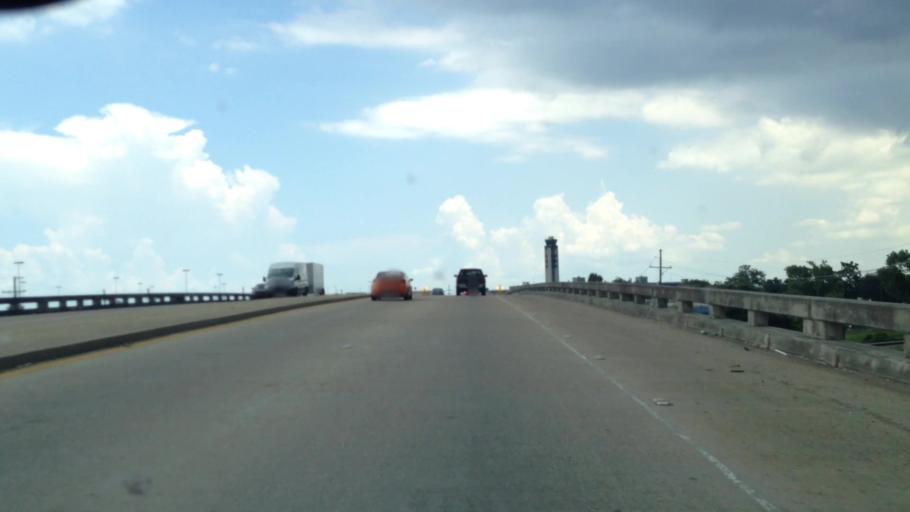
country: US
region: Louisiana
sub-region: Jefferson Parish
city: Kenner
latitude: 29.9825
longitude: -90.2678
